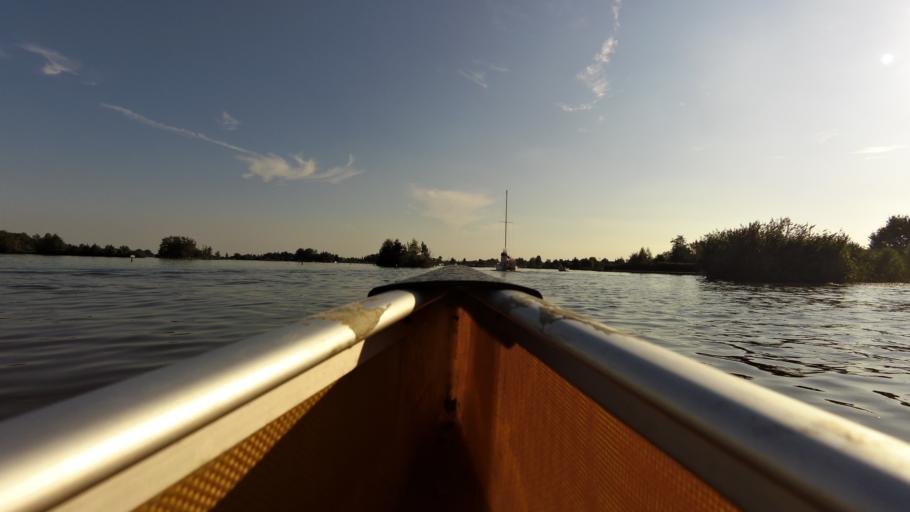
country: NL
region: South Holland
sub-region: Gemeente Nieuwkoop
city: Nieuwkoop
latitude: 52.1416
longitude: 4.7722
